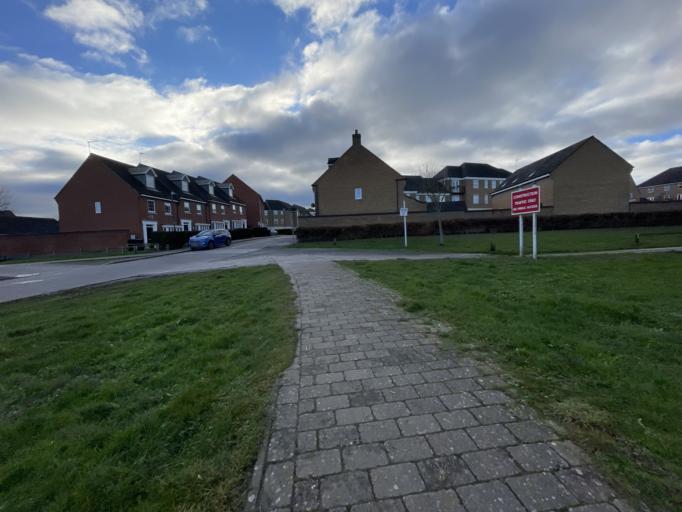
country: GB
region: England
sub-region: Warwickshire
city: Rugby
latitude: 52.3992
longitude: -1.2375
